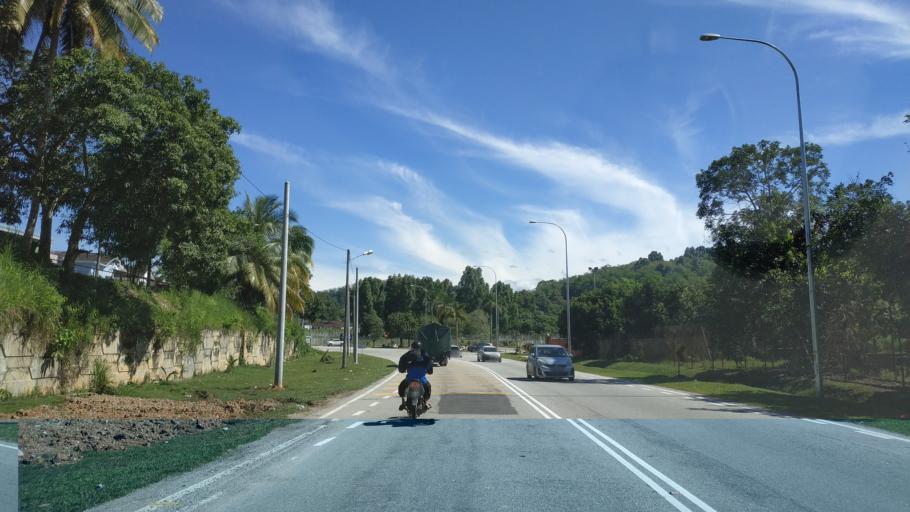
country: MY
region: Kedah
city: Kulim
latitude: 5.3346
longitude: 100.5365
